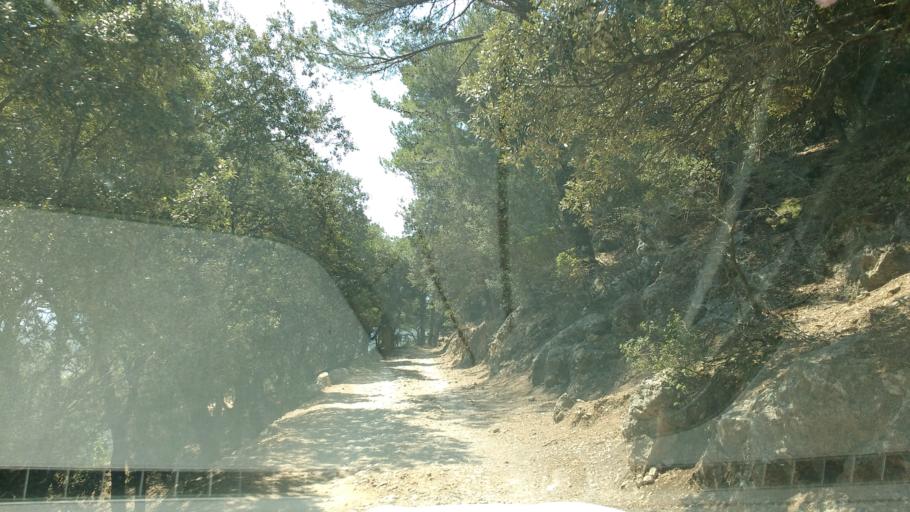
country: ES
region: Balearic Islands
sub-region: Illes Balears
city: Alaro
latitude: 39.7297
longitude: 2.7871
